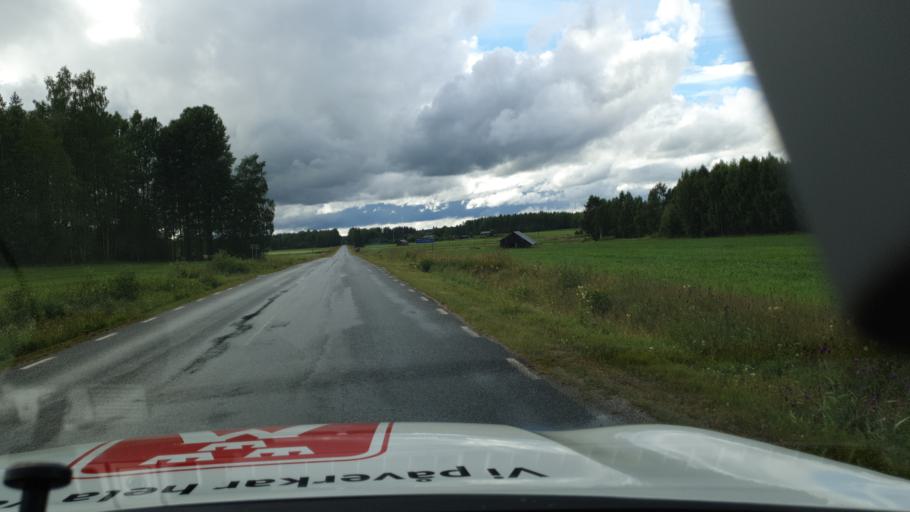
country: SE
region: Vaesterbotten
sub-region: Skelleftea Kommun
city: Viken
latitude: 64.5832
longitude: 20.9857
